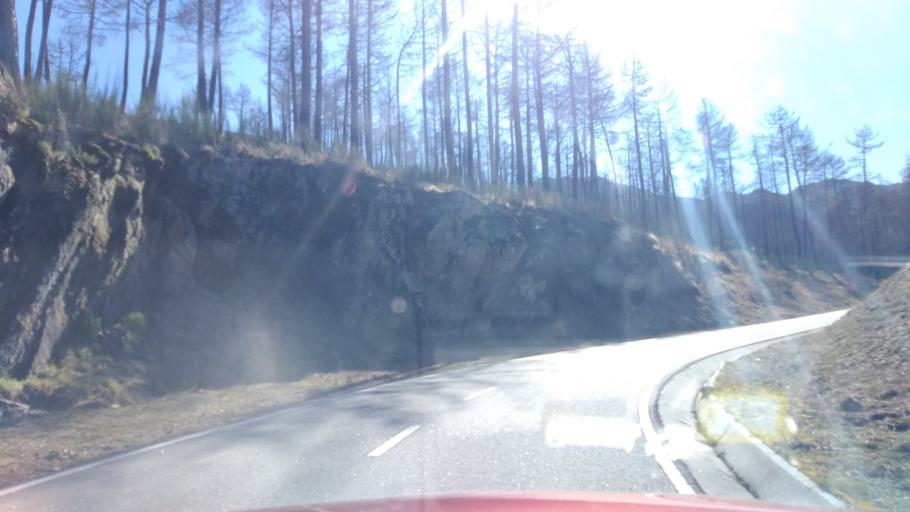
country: PT
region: Guarda
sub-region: Manteigas
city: Manteigas
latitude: 40.4919
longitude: -7.5218
